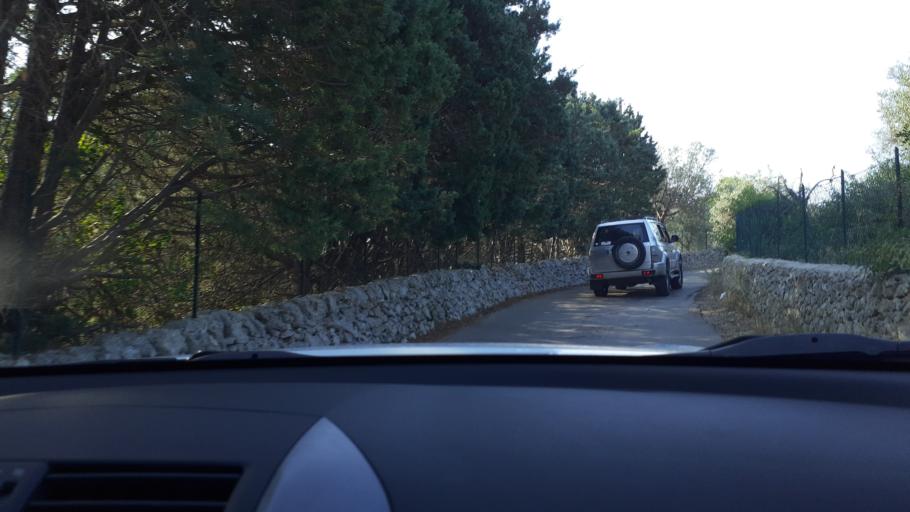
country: IT
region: Sicily
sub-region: Provincia di Siracusa
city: Cassibile
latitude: 36.9763
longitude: 15.1585
